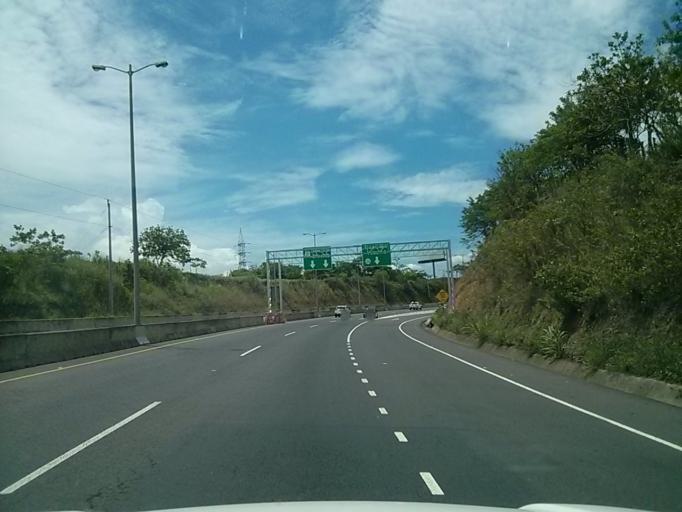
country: CR
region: Heredia
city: Colon
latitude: 9.9657
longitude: -84.2537
